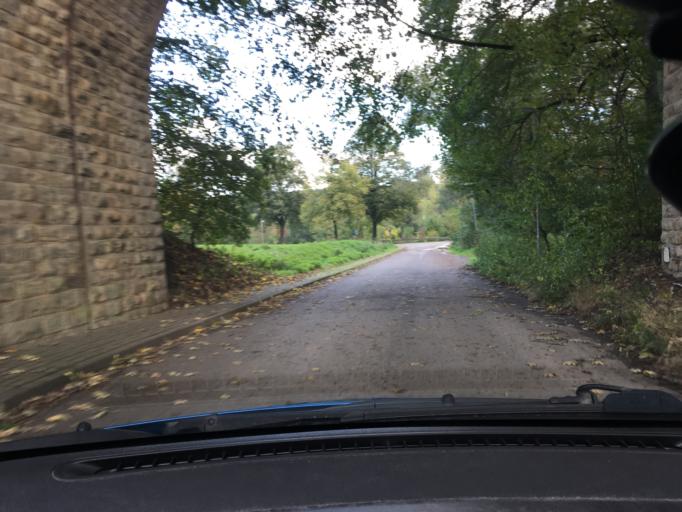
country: DE
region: Lower Saxony
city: Bad Munder am Deister
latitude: 52.1819
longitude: 9.4680
